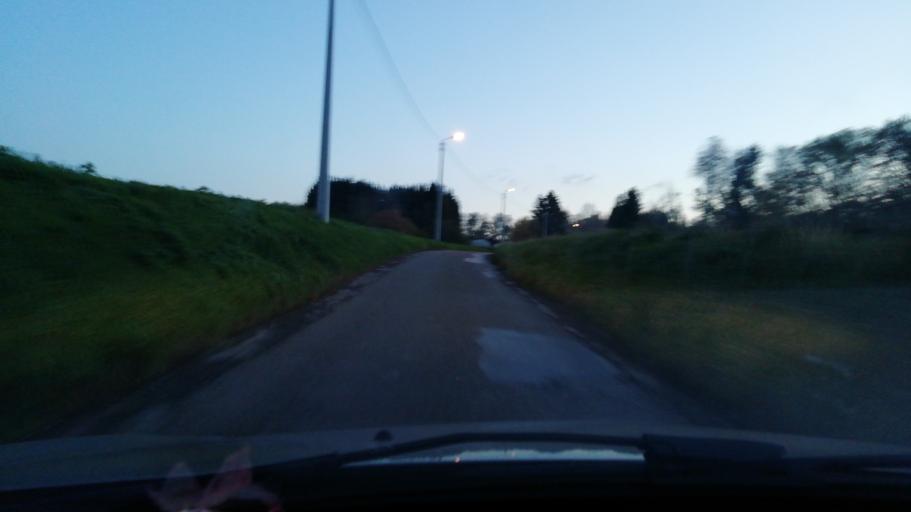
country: FR
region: Nord-Pas-de-Calais
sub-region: Departement du Nord
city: Marpent
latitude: 50.2799
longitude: 4.0893
